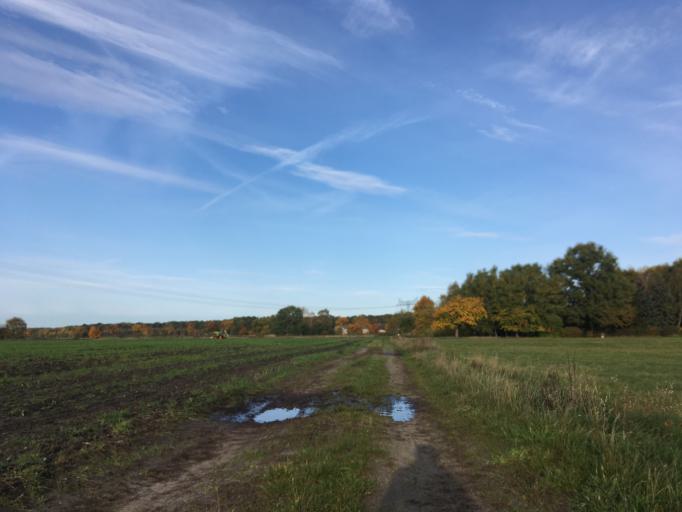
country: DE
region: Berlin
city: Buch
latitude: 52.6788
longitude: 13.4673
